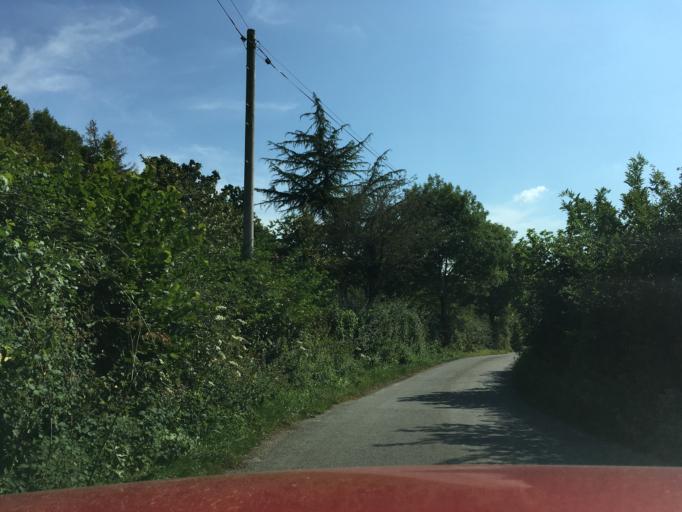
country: GB
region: England
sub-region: Gloucestershire
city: Dursley
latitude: 51.7050
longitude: -2.3144
